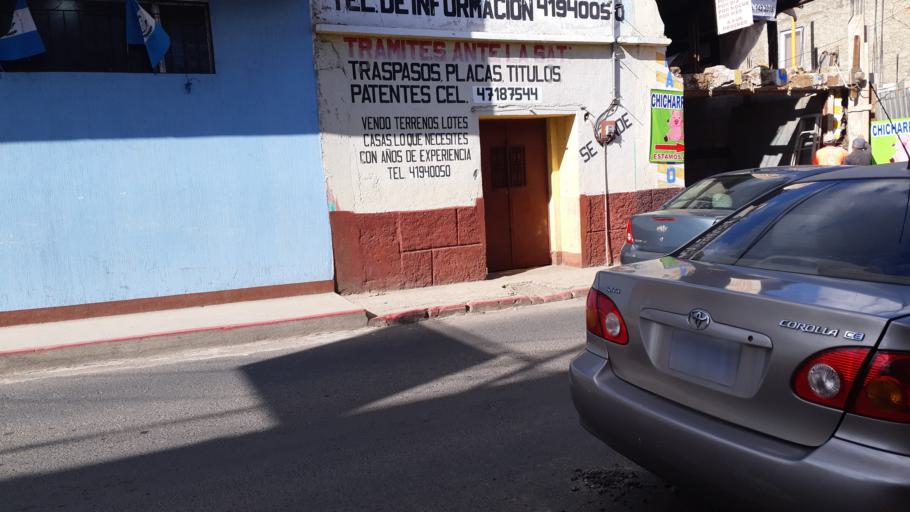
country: GT
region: Chimaltenango
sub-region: Municipio de Chimaltenango
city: Chimaltenango
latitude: 14.6610
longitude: -90.8240
